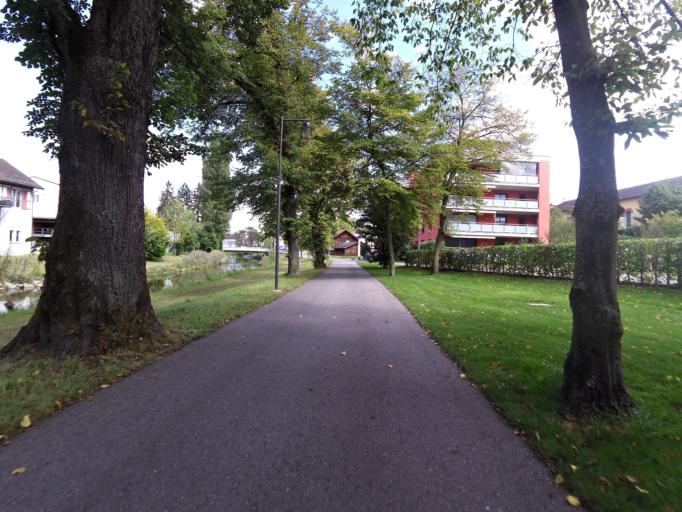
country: CH
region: Thurgau
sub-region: Frauenfeld District
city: Frauenfeld
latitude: 47.5596
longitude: 8.8969
